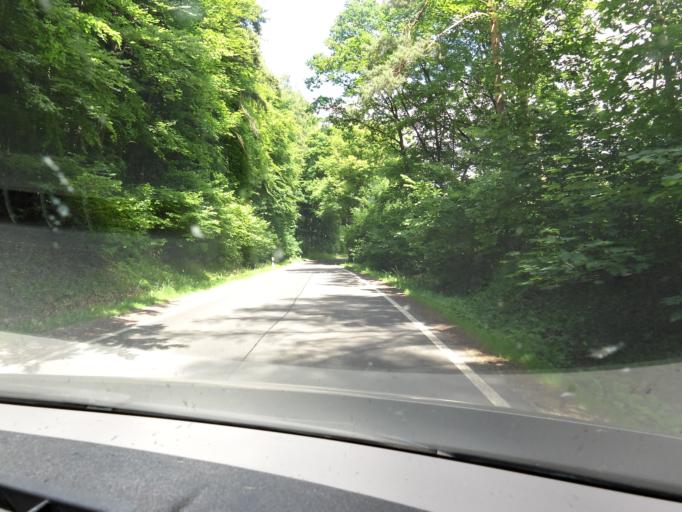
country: DE
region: Thuringia
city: Ernstroda
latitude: 50.8538
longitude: 10.6184
